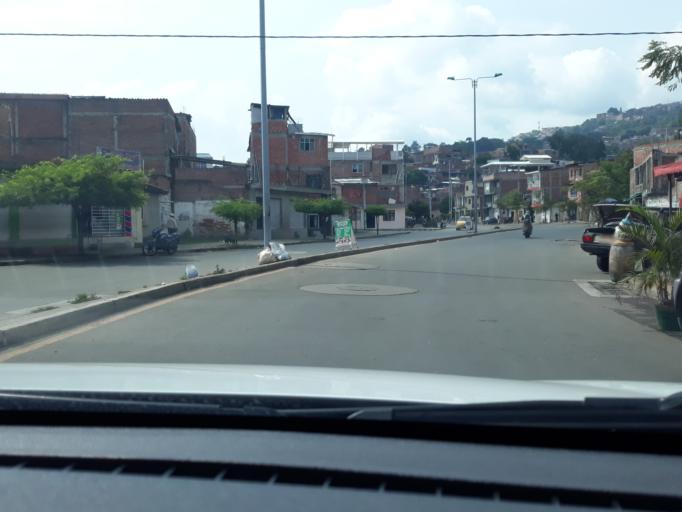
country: CO
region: Valle del Cauca
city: Cali
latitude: 3.3910
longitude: -76.5565
